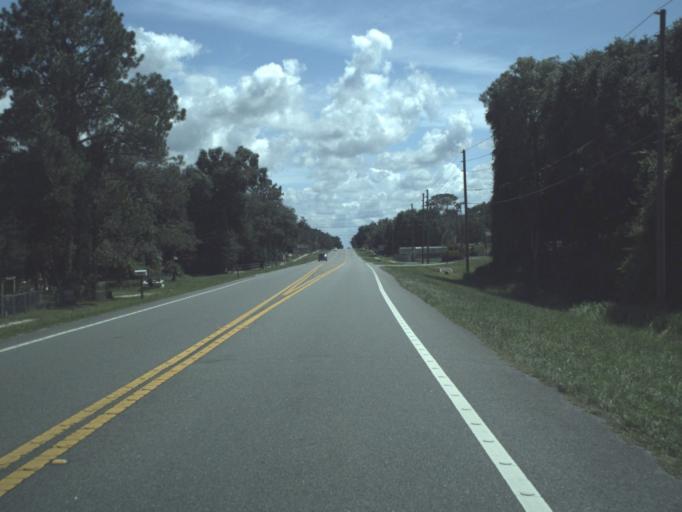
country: US
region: Florida
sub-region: Citrus County
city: Hernando
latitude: 28.9341
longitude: -82.3773
